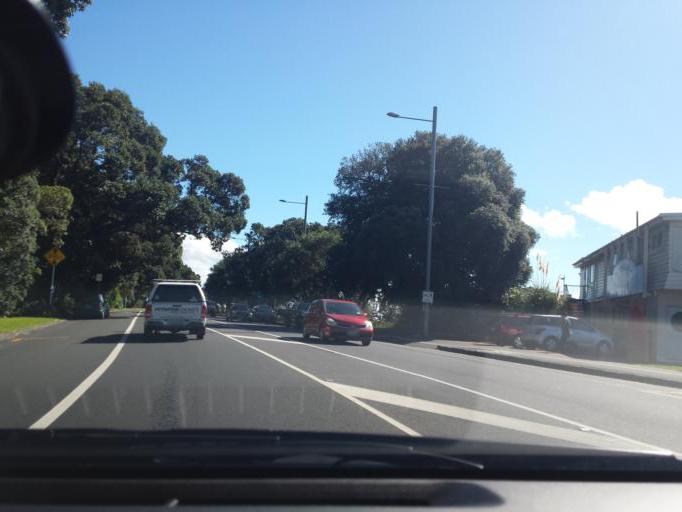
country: NZ
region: Auckland
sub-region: Auckland
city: Auckland
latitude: -36.8515
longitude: 174.8132
